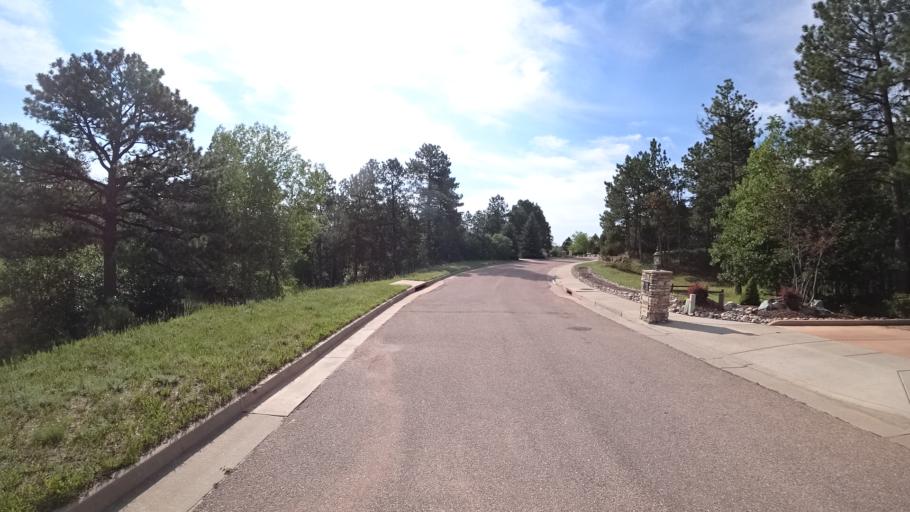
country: US
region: Colorado
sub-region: El Paso County
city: Air Force Academy
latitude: 38.9448
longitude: -104.8283
